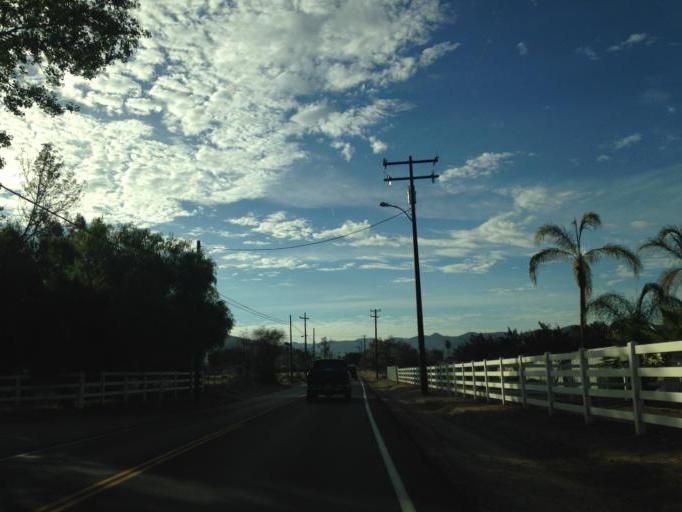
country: US
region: California
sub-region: San Diego County
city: Rainbow
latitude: 33.3759
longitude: -117.0801
